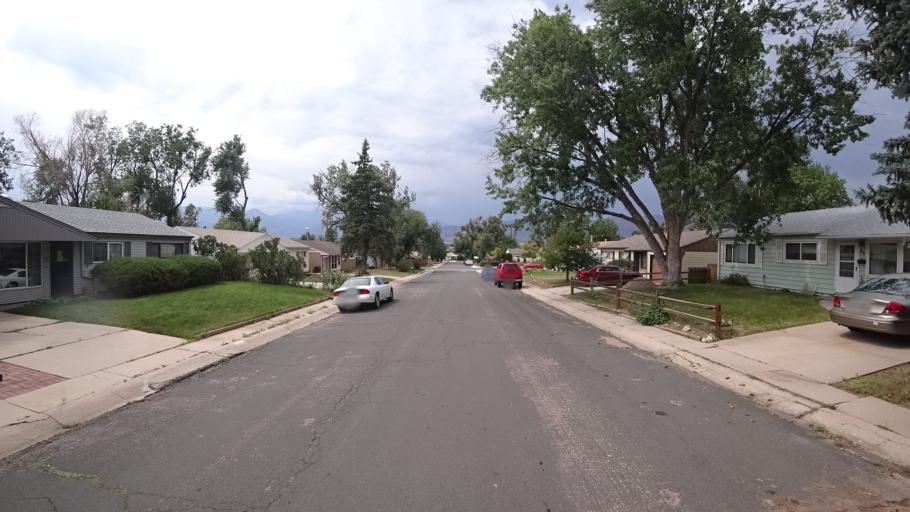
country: US
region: Colorado
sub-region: El Paso County
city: Colorado Springs
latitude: 38.8957
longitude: -104.8145
